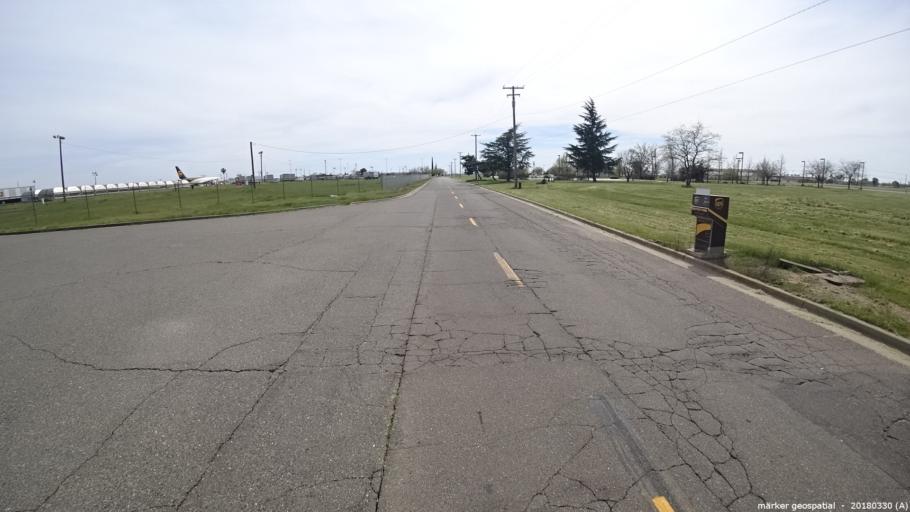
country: US
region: California
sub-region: Sacramento County
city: Rancho Cordova
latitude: 38.5628
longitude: -121.3100
